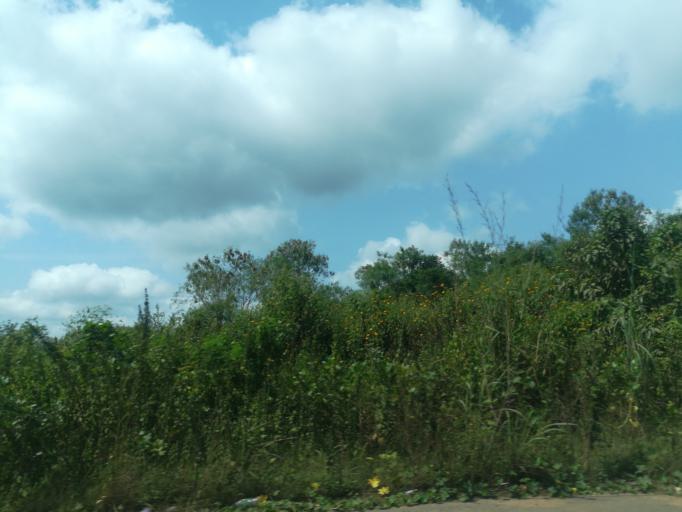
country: NG
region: Oyo
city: Moniya
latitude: 7.5891
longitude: 3.9138
